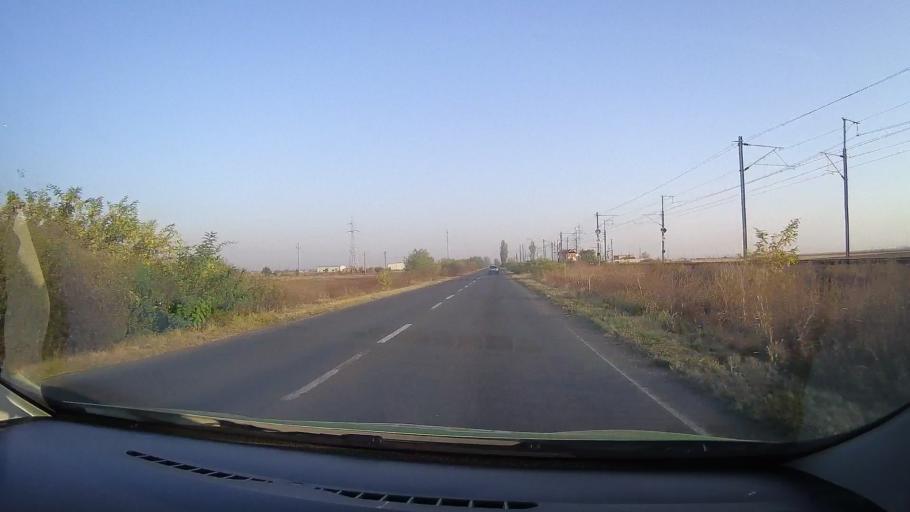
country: RO
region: Arad
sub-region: Comuna Sofronea
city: Sofronea
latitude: 46.2594
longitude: 21.3176
